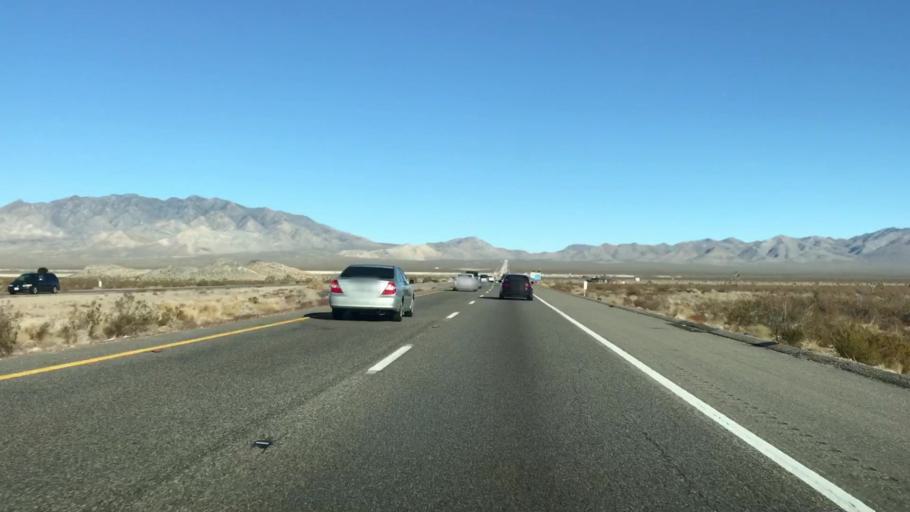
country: US
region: Nevada
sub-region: Clark County
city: Sandy Valley
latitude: 35.4319
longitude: -115.7141
